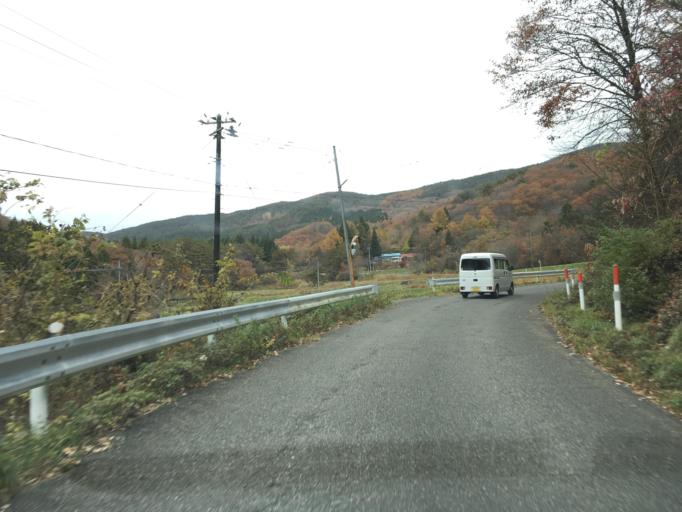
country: JP
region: Iwate
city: Mizusawa
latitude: 39.1146
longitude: 141.3255
